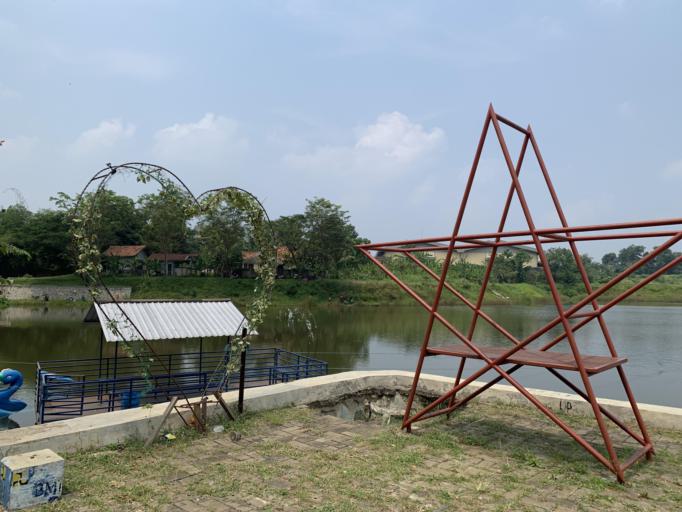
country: ID
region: West Java
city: Cikupa
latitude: -6.3209
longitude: 106.4702
